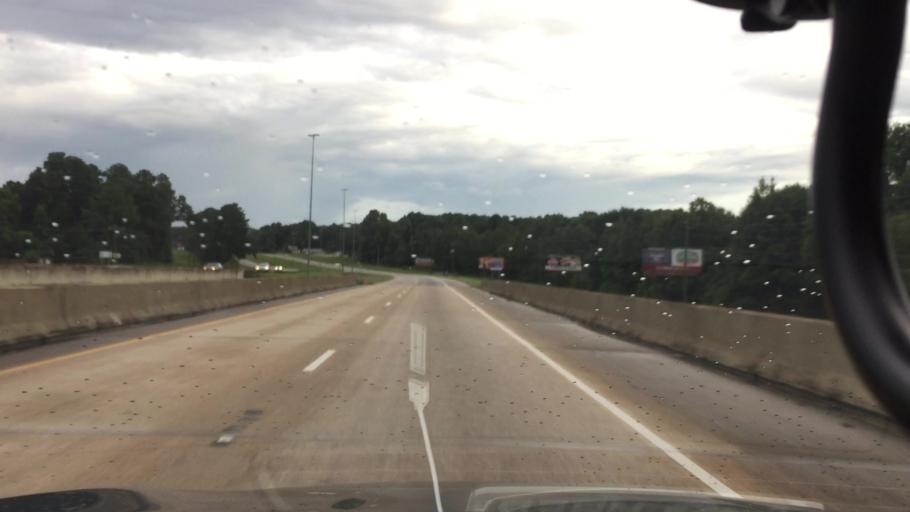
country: US
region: Alabama
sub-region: Pike County
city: Troy
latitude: 31.8447
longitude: -85.9949
